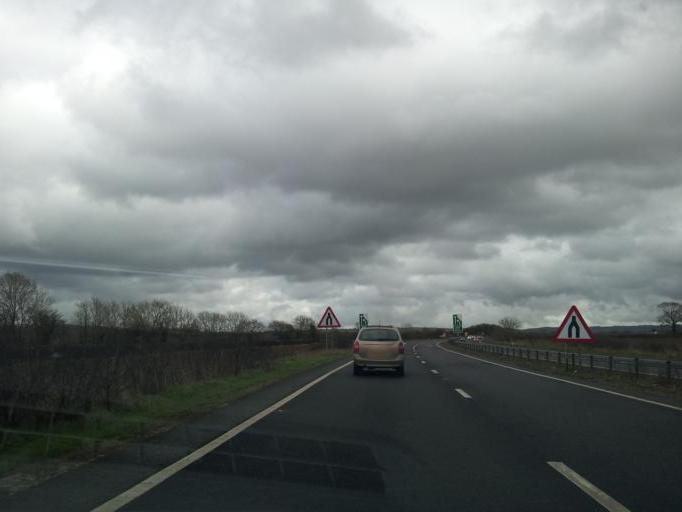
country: GB
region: England
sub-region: Somerset
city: Ilchester
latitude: 51.0242
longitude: -2.6457
